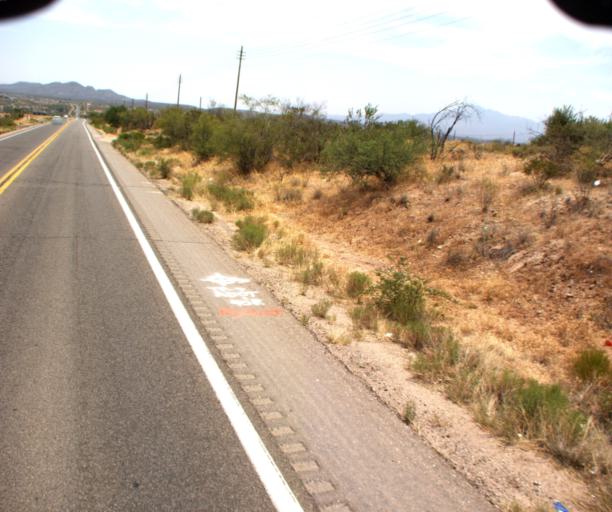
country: US
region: Arizona
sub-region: Gila County
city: Peridot
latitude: 33.3009
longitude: -110.4684
